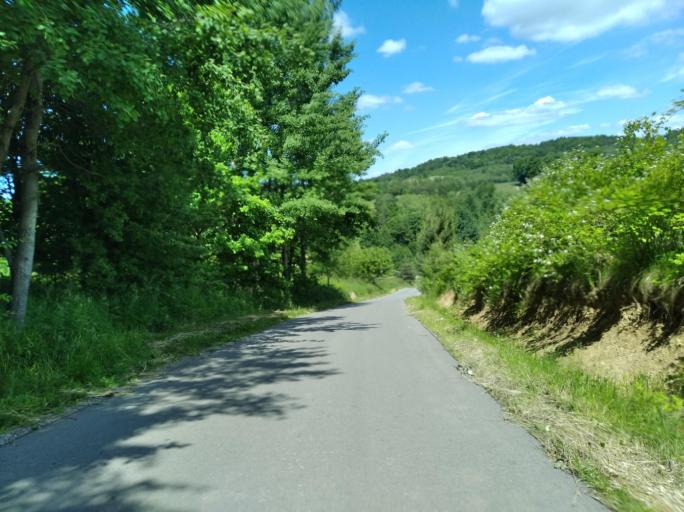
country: PL
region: Subcarpathian Voivodeship
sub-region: Powiat strzyzowski
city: Wysoka Strzyzowska
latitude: 49.7907
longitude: 21.7203
